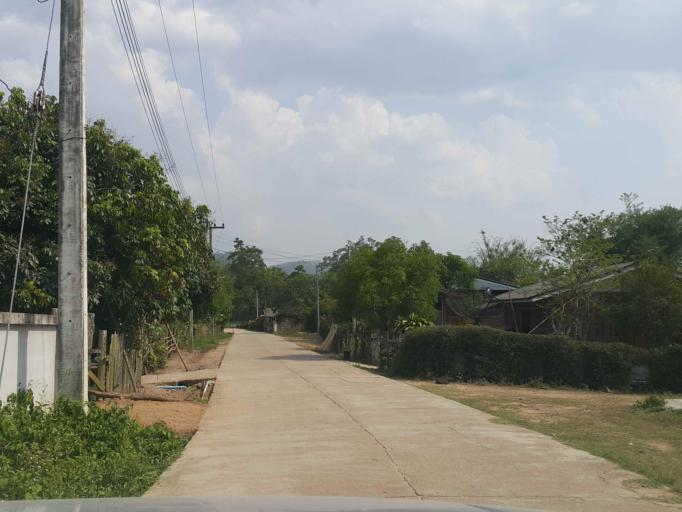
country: TH
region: Chiang Mai
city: Wiang Haeng
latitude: 19.3940
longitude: 98.7218
